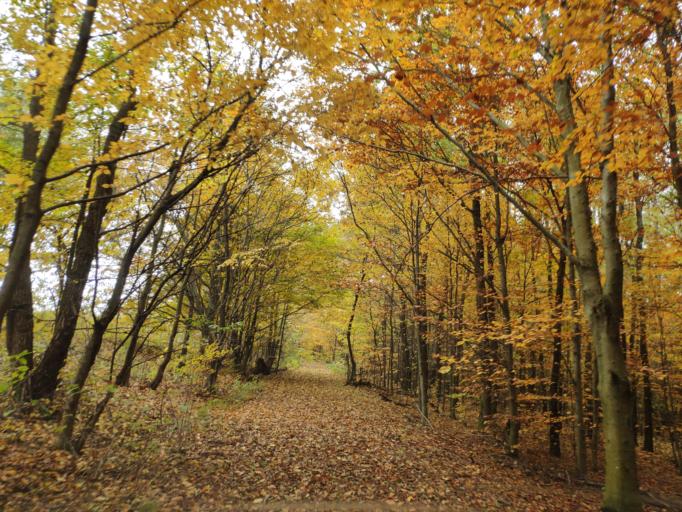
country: SK
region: Kosicky
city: Moldava nad Bodvou
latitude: 48.7251
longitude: 21.0965
